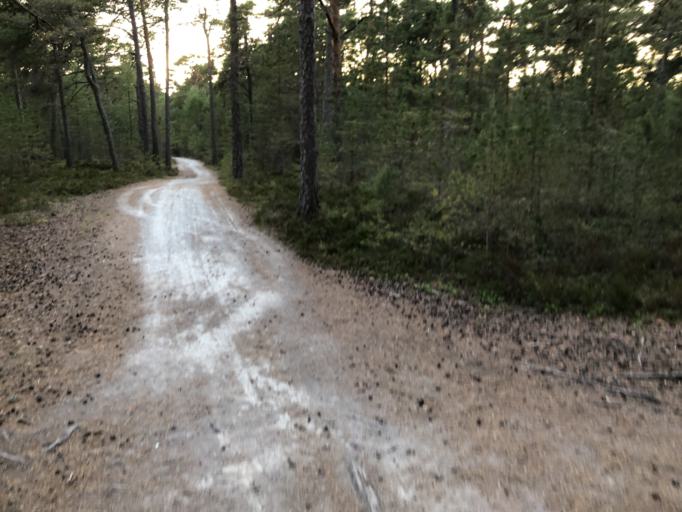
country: EE
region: Harju
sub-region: Paldiski linn
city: Paldiski
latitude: 59.3904
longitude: 24.2221
